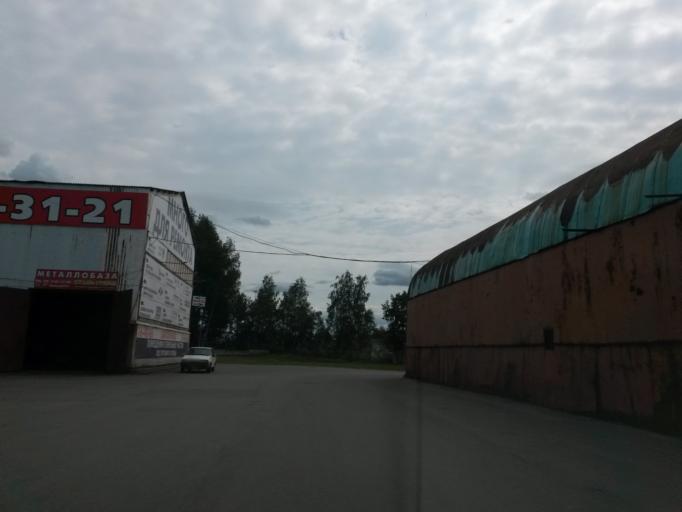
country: RU
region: Jaroslavl
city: Yaroslavl
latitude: 57.6867
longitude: 39.9063
